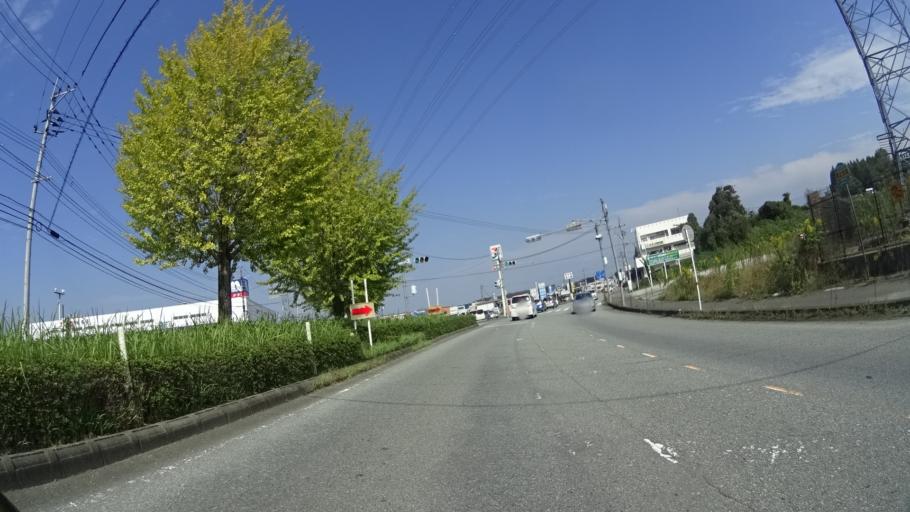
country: JP
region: Kumamoto
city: Uto
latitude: 32.6961
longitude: 130.7267
